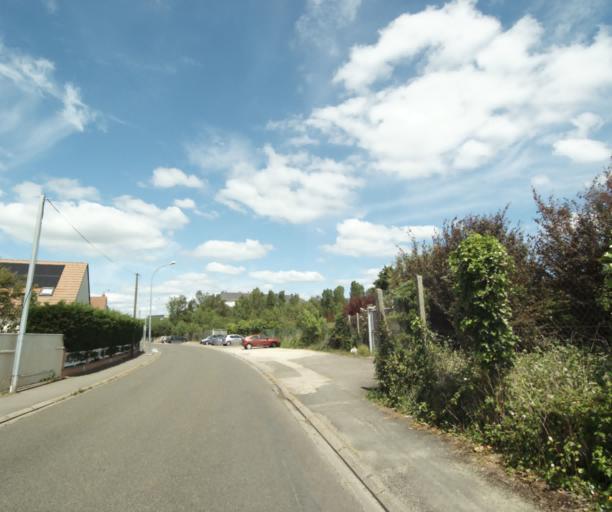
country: FR
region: Centre
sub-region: Departement d'Eure-et-Loir
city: Luce
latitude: 48.4368
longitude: 1.4678
